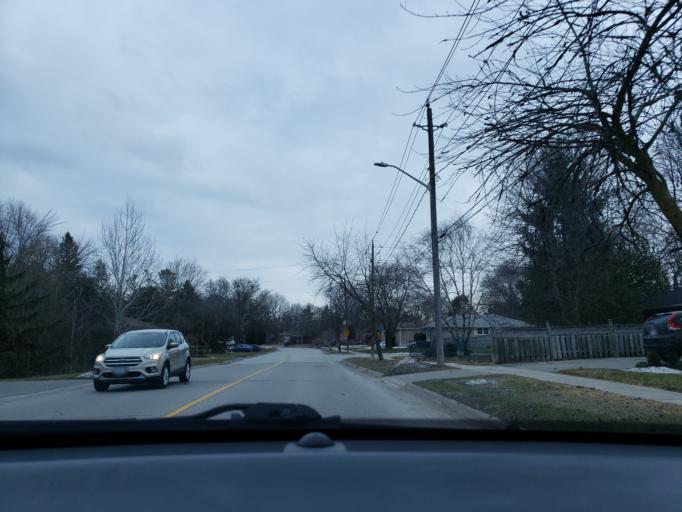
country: CA
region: Ontario
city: Newmarket
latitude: 44.0507
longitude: -79.4741
